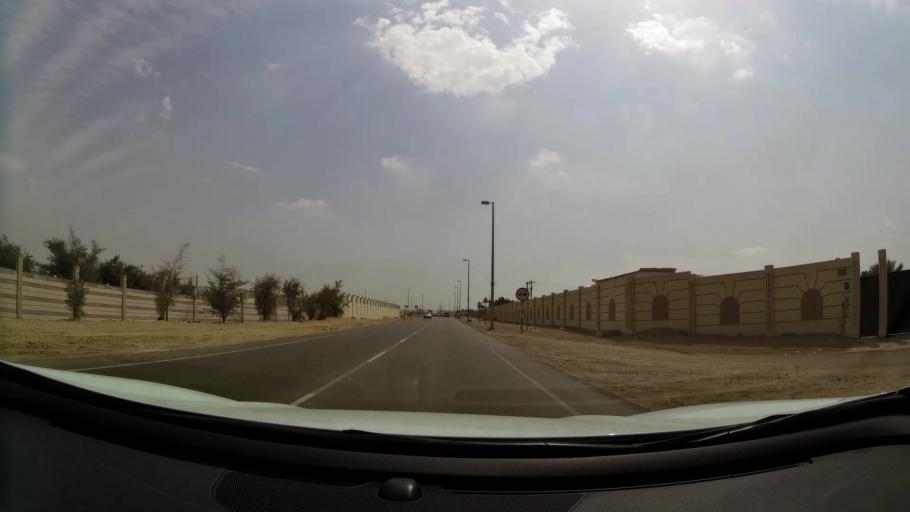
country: AE
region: Abu Dhabi
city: Abu Dhabi
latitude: 24.5164
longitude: 54.6569
